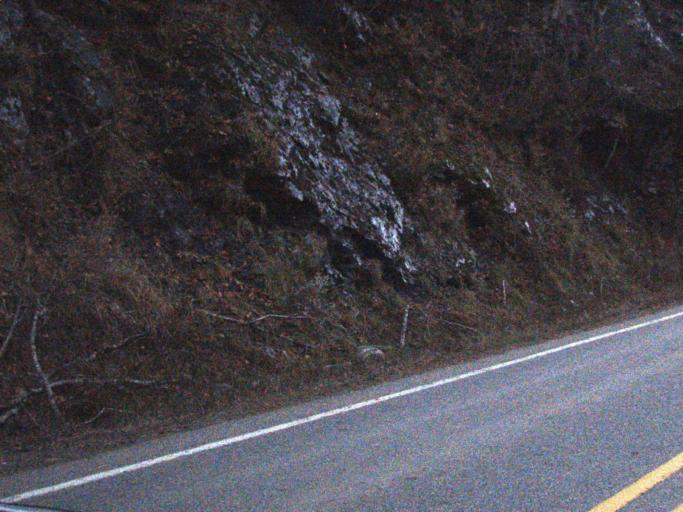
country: US
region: Washington
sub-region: Snohomish County
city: Darrington
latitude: 48.7054
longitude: -121.1766
